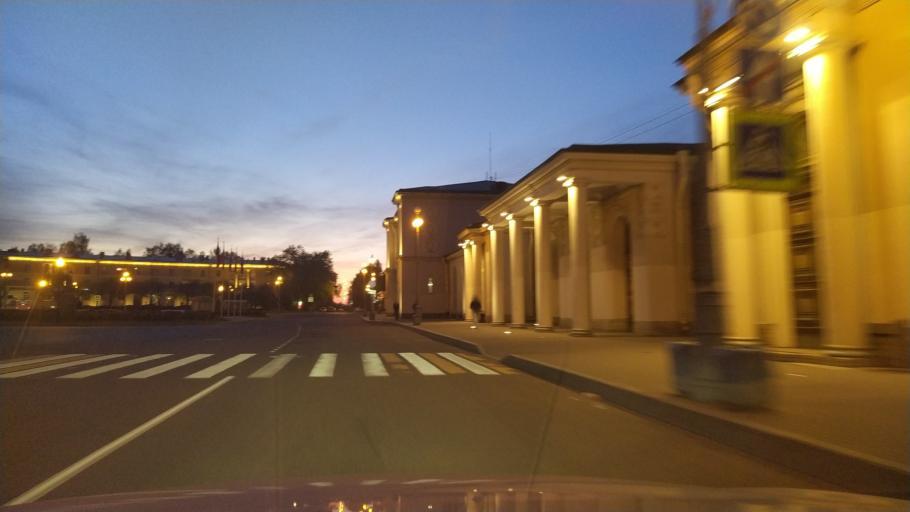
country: RU
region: St.-Petersburg
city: Pushkin
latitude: 59.7223
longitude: 30.4293
